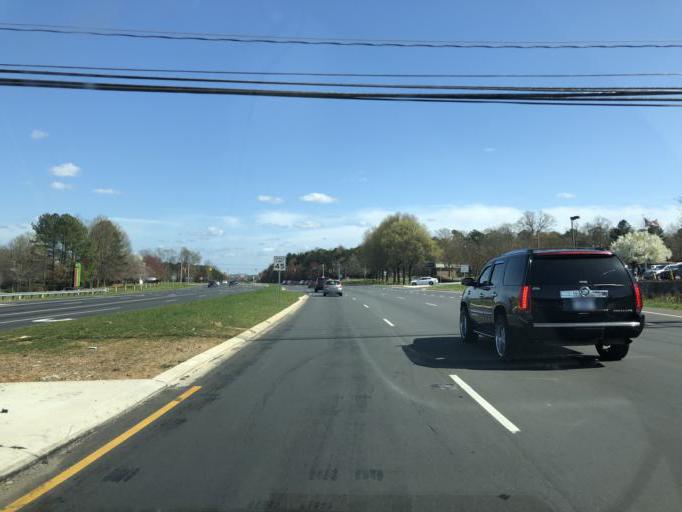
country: US
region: North Carolina
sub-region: Mecklenburg County
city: Charlotte
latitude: 35.3184
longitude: -80.7788
